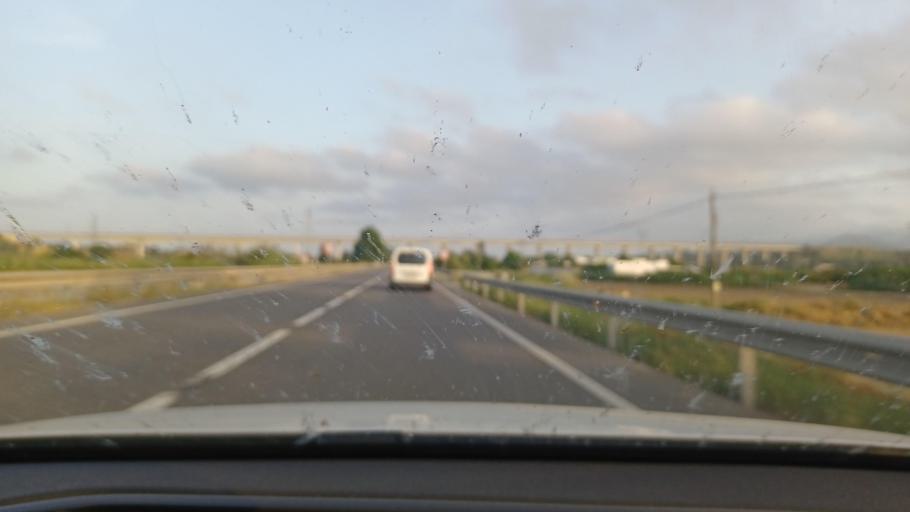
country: ES
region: Catalonia
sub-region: Provincia de Tarragona
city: Amposta
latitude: 40.7359
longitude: 0.5676
